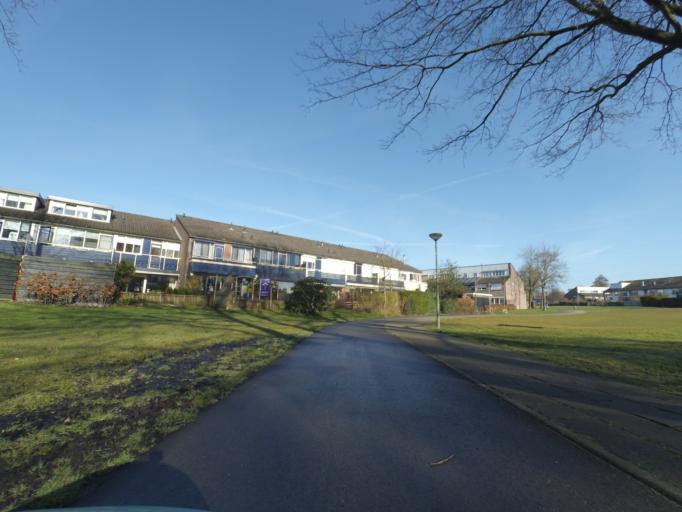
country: NL
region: Gelderland
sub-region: Gemeente Barneveld
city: Barneveld
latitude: 52.1305
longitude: 5.5776
